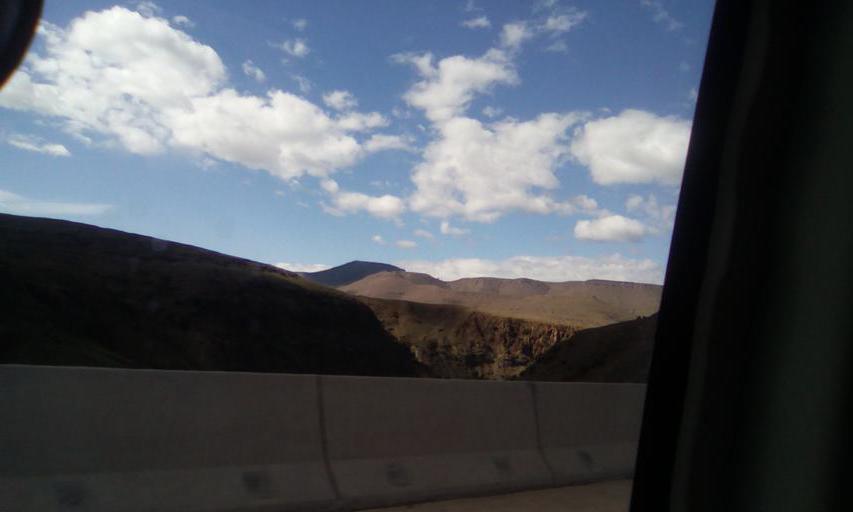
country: LS
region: Qacha's Nek
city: Qacha's Nek
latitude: -30.0240
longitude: 28.1818
